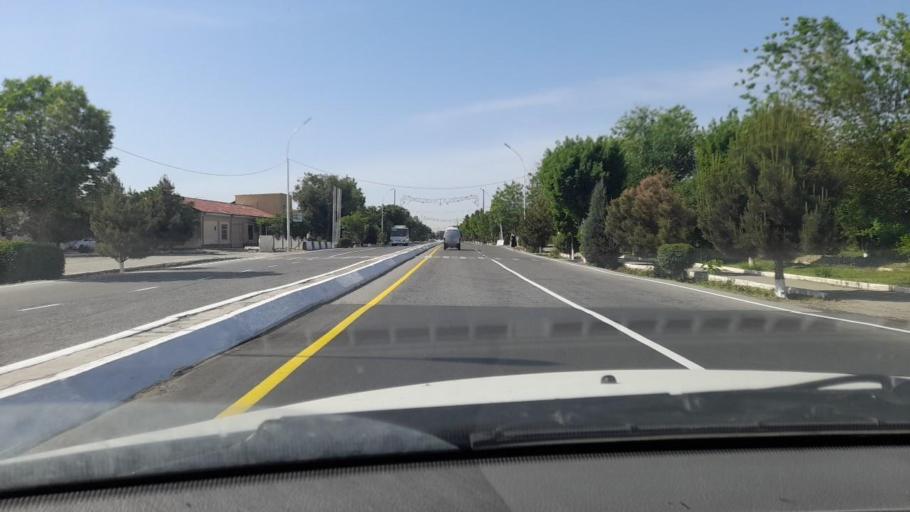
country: UZ
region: Bukhara
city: Bukhara
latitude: 39.7946
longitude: 64.4344
